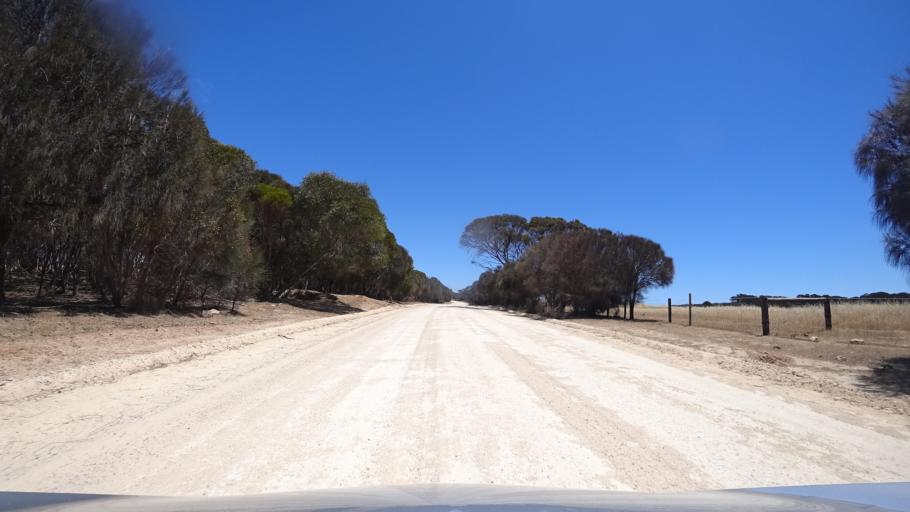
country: AU
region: South Australia
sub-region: Kangaroo Island
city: Kingscote
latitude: -35.6290
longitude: 137.1990
